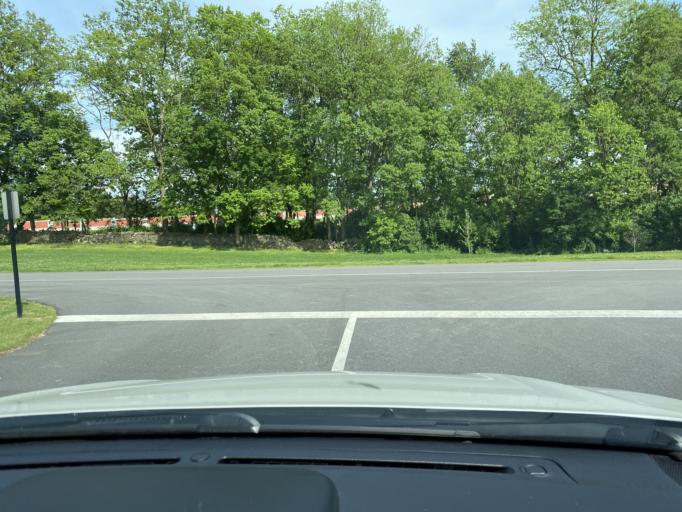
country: US
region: Kentucky
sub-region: Scott County
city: Georgetown
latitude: 38.2148
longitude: -84.5977
